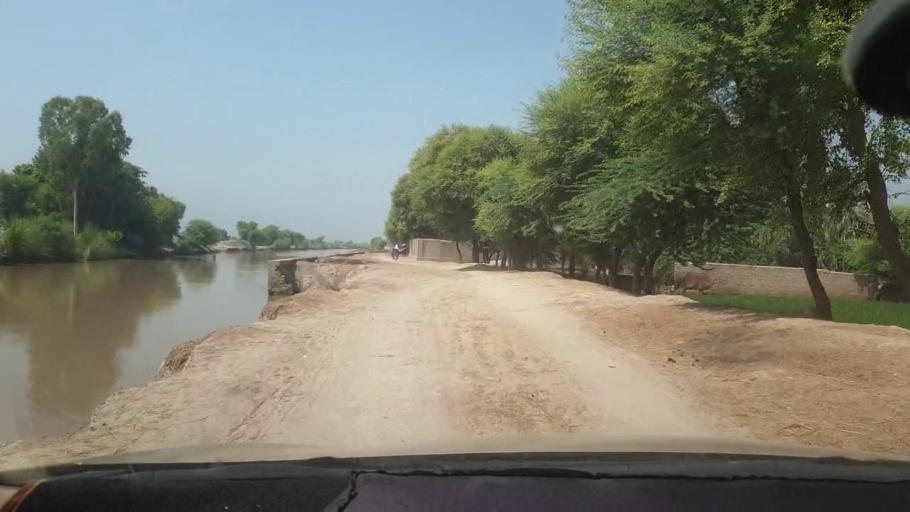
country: PK
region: Sindh
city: Shahdadkot
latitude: 27.7142
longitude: 67.9363
